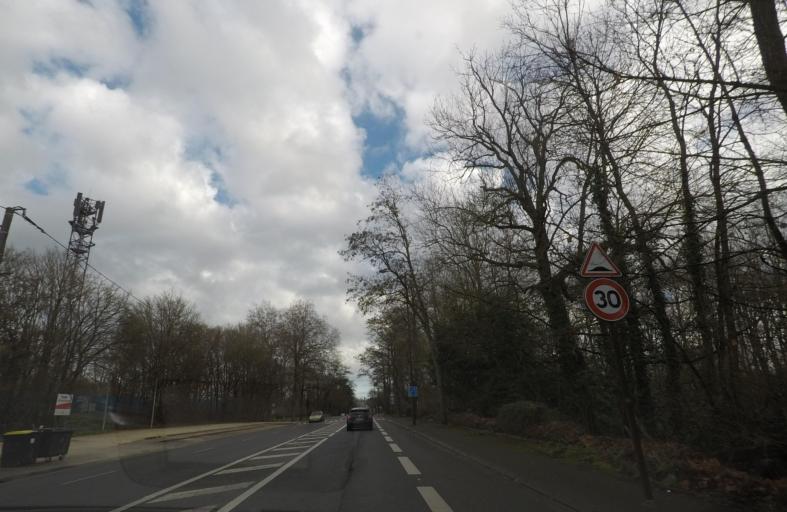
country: FR
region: Centre
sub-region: Departement du Cher
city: Bourges
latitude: 47.0717
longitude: 2.3913
